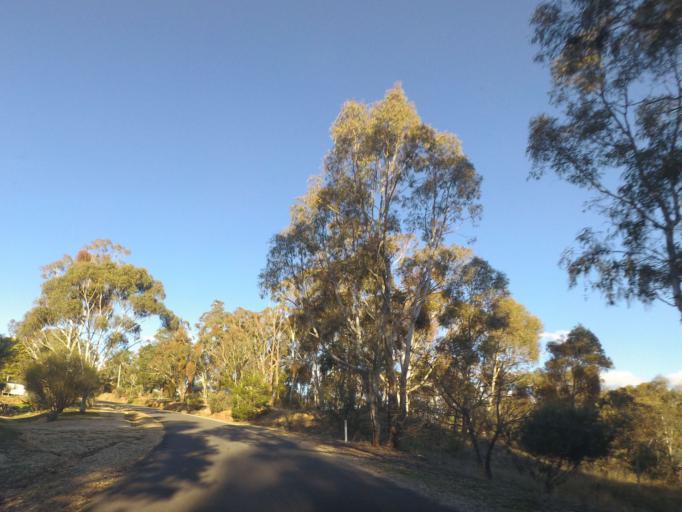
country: AU
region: Victoria
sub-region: Mount Alexander
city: Castlemaine
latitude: -37.1581
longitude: 144.2114
